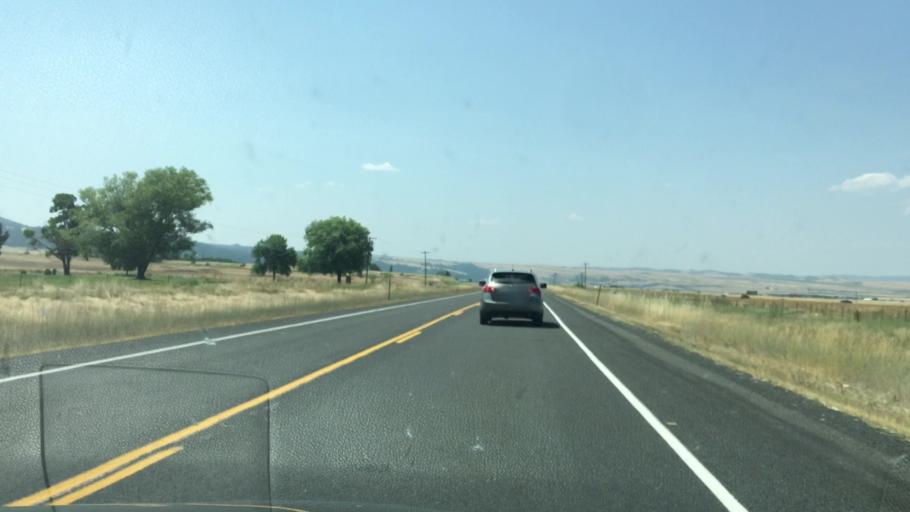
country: US
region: Idaho
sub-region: Idaho County
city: Grangeville
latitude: 45.9121
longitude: -116.1631
